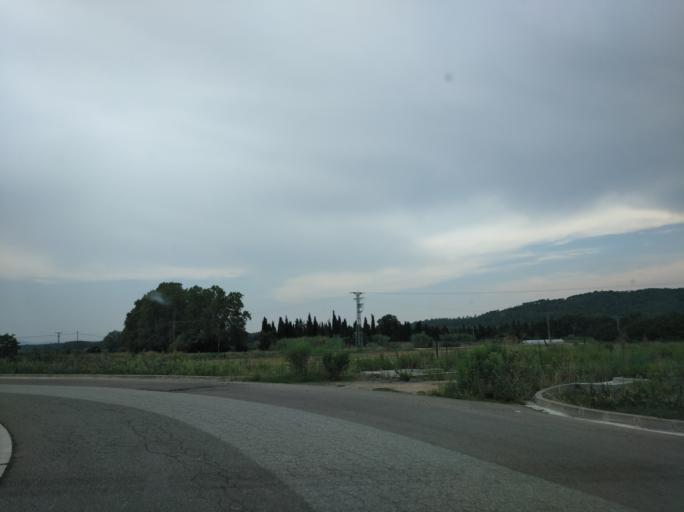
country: ES
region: Catalonia
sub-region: Provincia de Girona
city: Santa Coloma de Farners
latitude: 41.8534
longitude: 2.6772
